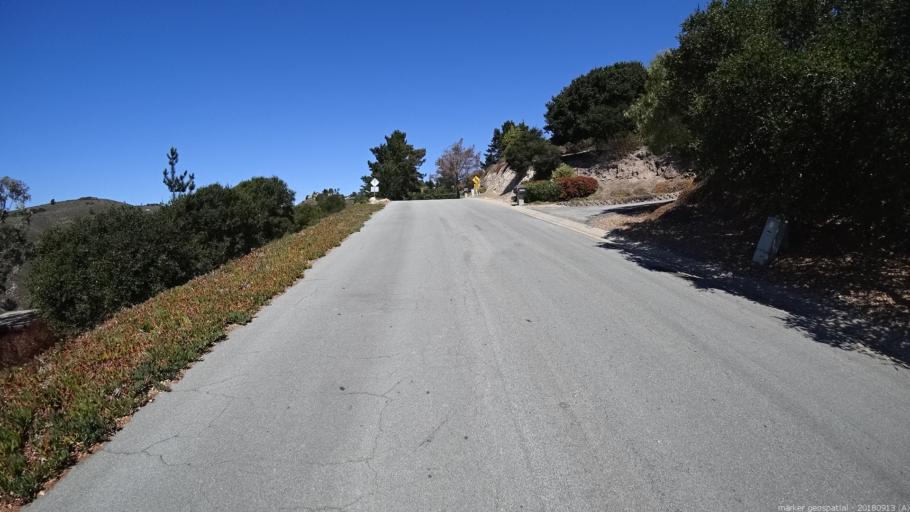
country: US
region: California
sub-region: Monterey County
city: Carmel Valley Village
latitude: 36.5295
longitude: -121.8026
